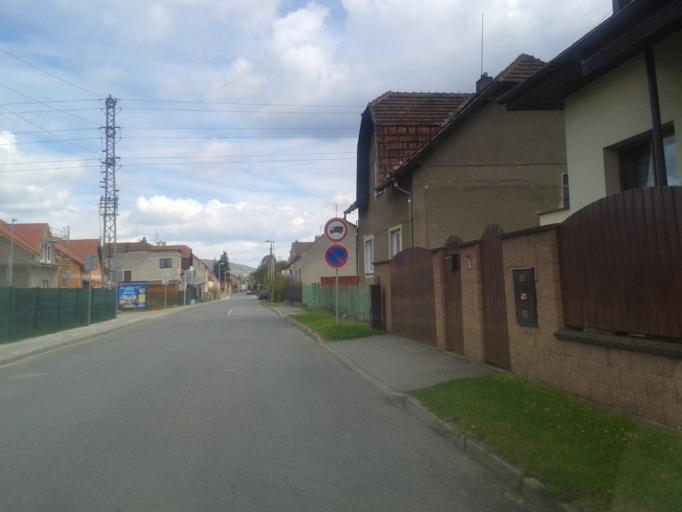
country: CZ
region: Central Bohemia
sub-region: Okres Beroun
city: Kraluv Dvur
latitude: 49.9335
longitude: 14.0248
